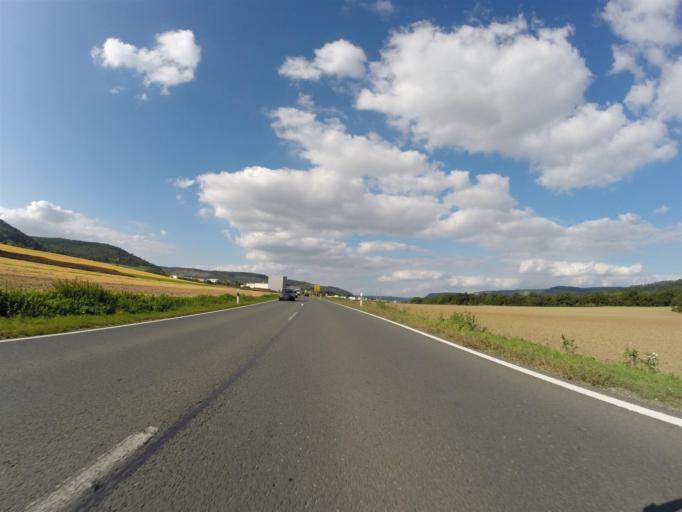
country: DE
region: Thuringia
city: Rothenstein
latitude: 50.8567
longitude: 11.6011
